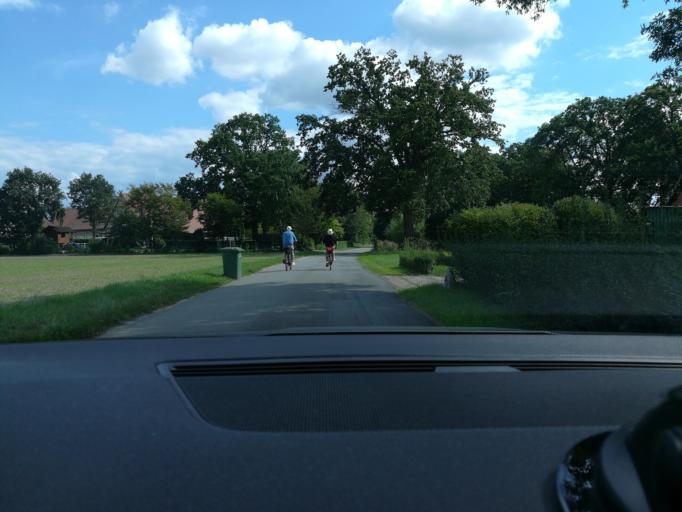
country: DE
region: North Rhine-Westphalia
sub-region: Regierungsbezirk Detmold
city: Huellhorst
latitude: 52.3391
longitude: 8.6813
